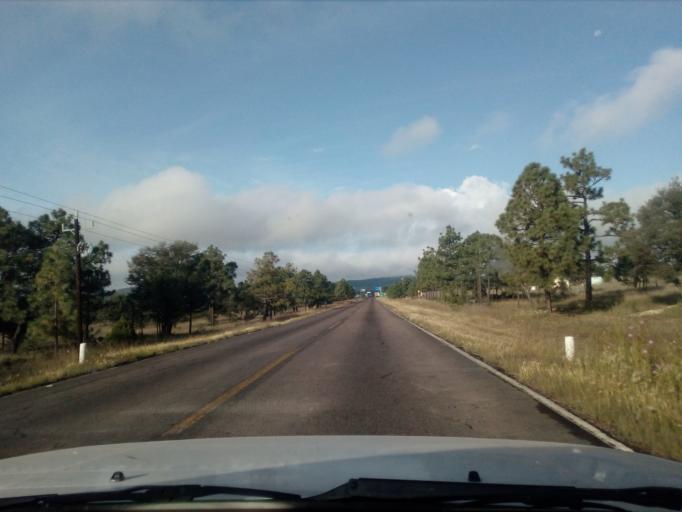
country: MX
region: Durango
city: Victoria de Durango
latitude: 23.9261
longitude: -104.9352
